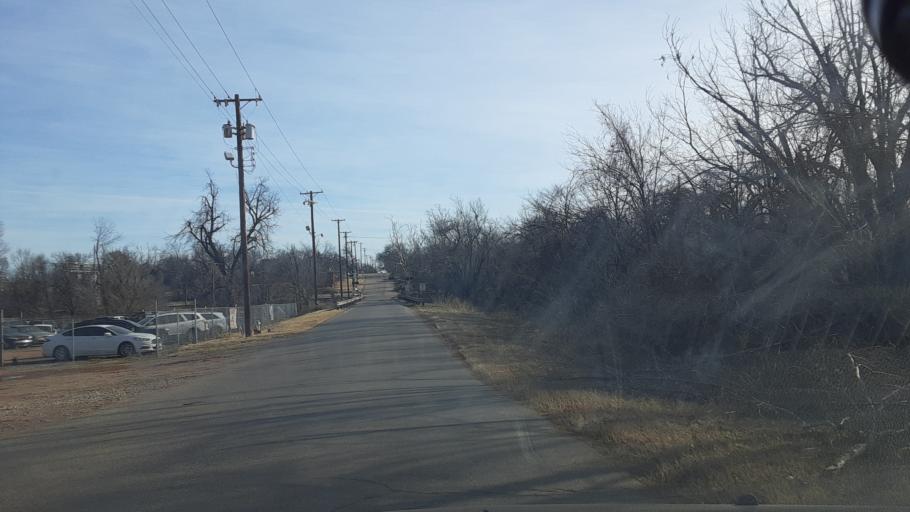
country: US
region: Oklahoma
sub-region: Logan County
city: Guthrie
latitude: 35.8853
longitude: -97.4272
